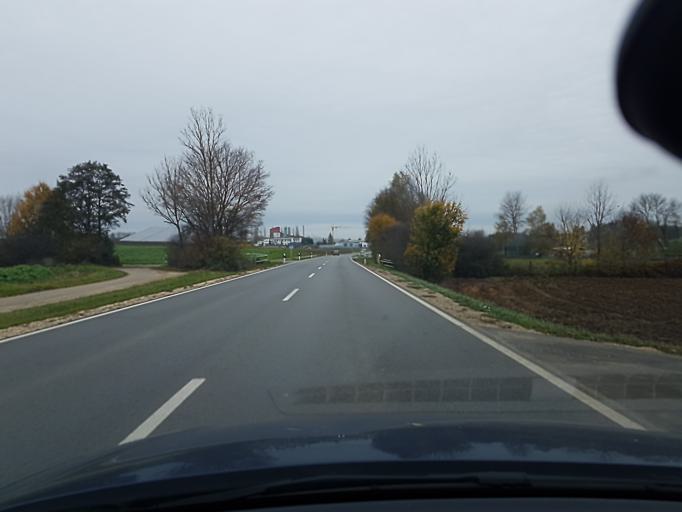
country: DE
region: Bavaria
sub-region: Lower Bavaria
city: Ergoldsbach
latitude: 48.7149
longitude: 12.1916
